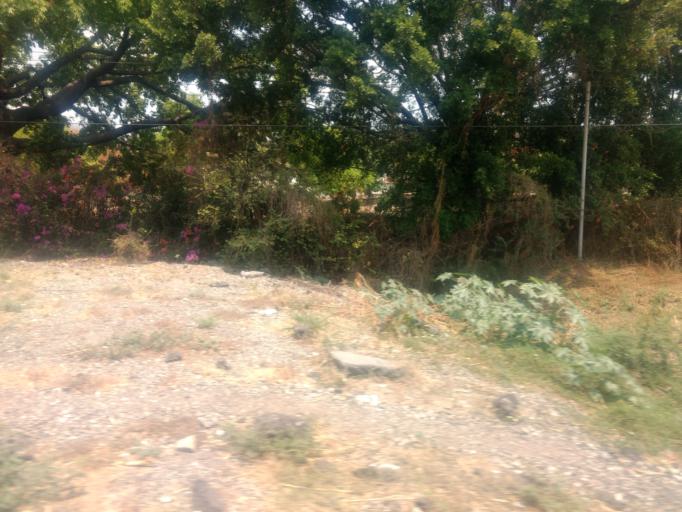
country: MX
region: Morelos
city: Puente de Ixtla
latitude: 18.6408
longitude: -99.3069
